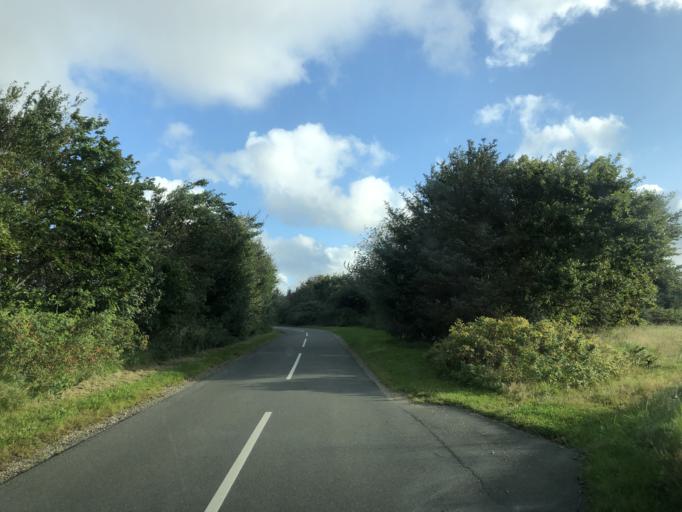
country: DK
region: Central Jutland
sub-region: Holstebro Kommune
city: Ulfborg
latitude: 56.3867
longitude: 8.3489
